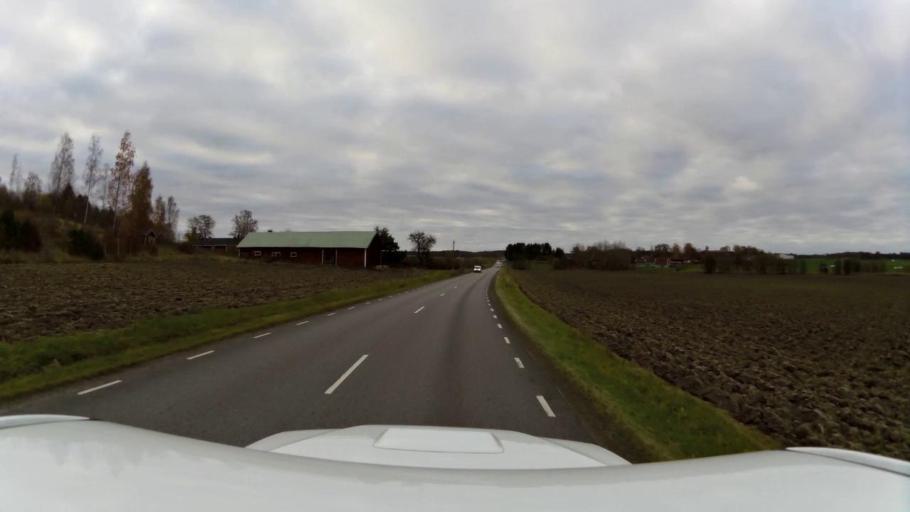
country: SE
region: OEstergoetland
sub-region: Linkopings Kommun
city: Linghem
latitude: 58.4037
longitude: 15.7652
